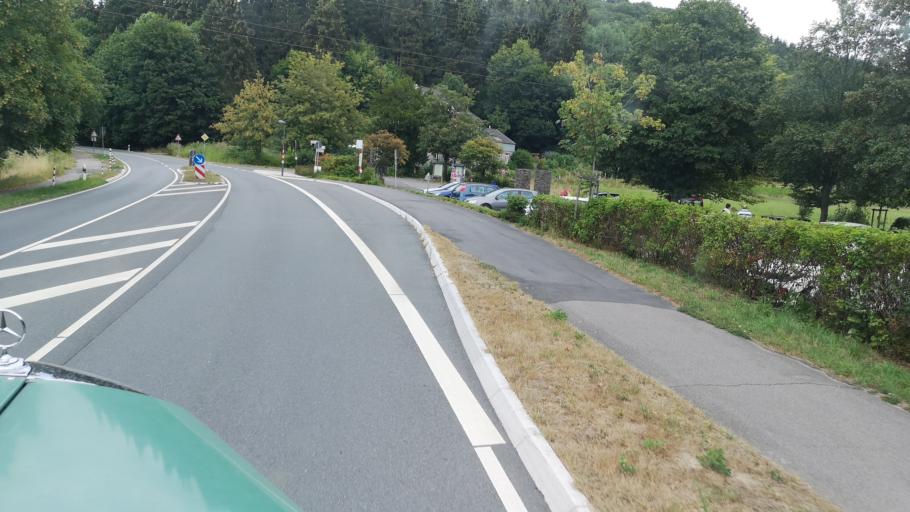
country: DE
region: North Rhine-Westphalia
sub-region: Regierungsbezirk Koln
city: Odenthal
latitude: 51.0633
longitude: 7.1416
